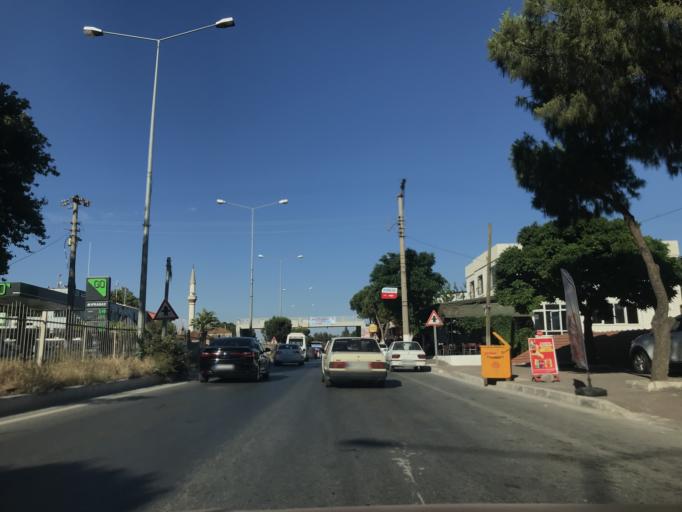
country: TR
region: Aydin
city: Soeke
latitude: 37.7832
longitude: 27.4610
